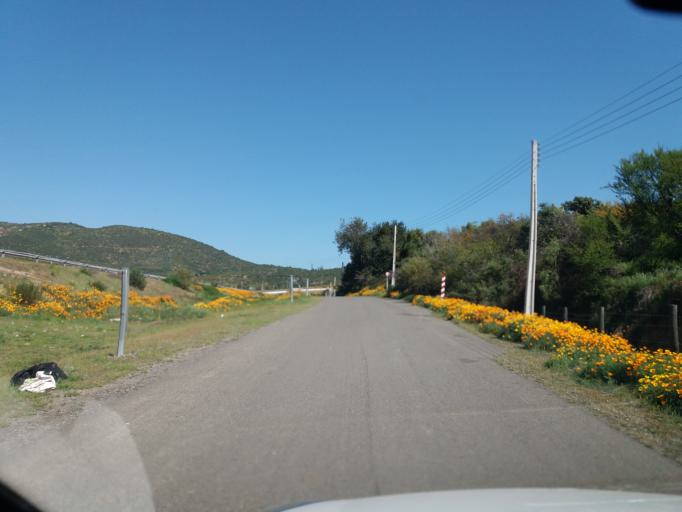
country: CL
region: Valparaiso
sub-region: Provincia de Quillota
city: Quillota
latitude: -32.9457
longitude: -71.2862
